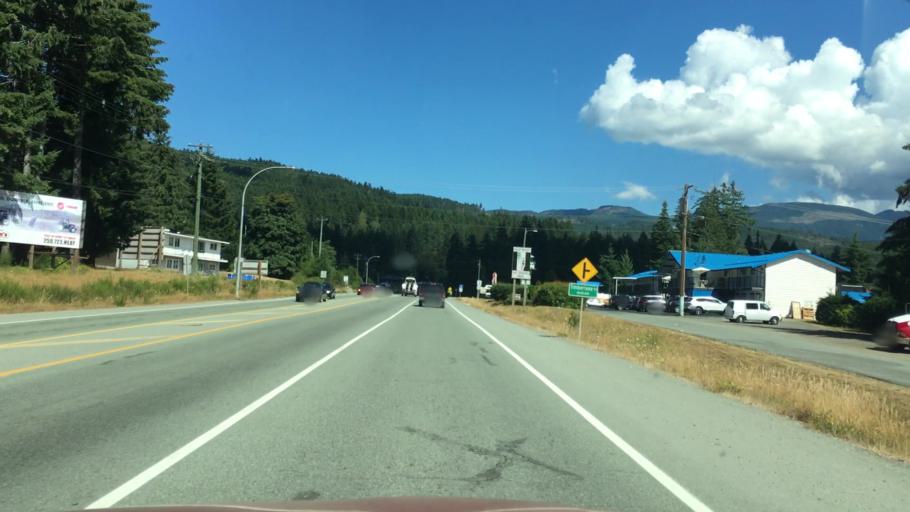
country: CA
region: British Columbia
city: Port Alberni
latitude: 49.2644
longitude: -124.7563
